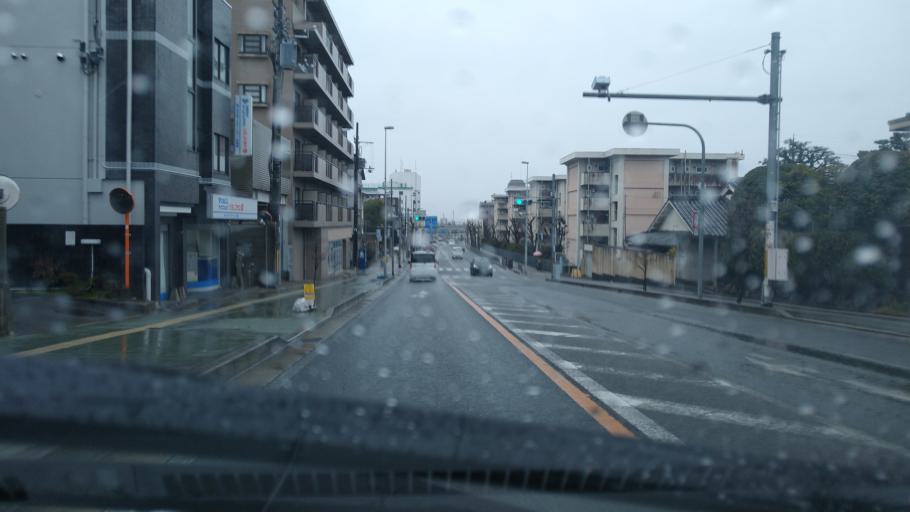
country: JP
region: Kyoto
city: Uji
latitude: 34.9322
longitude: 135.7681
